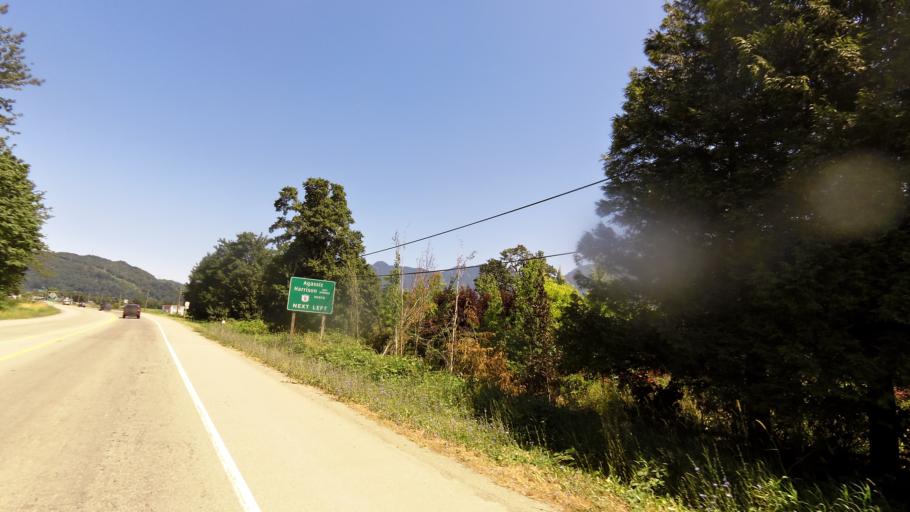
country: CA
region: British Columbia
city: Agassiz
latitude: 49.2204
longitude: -121.7728
